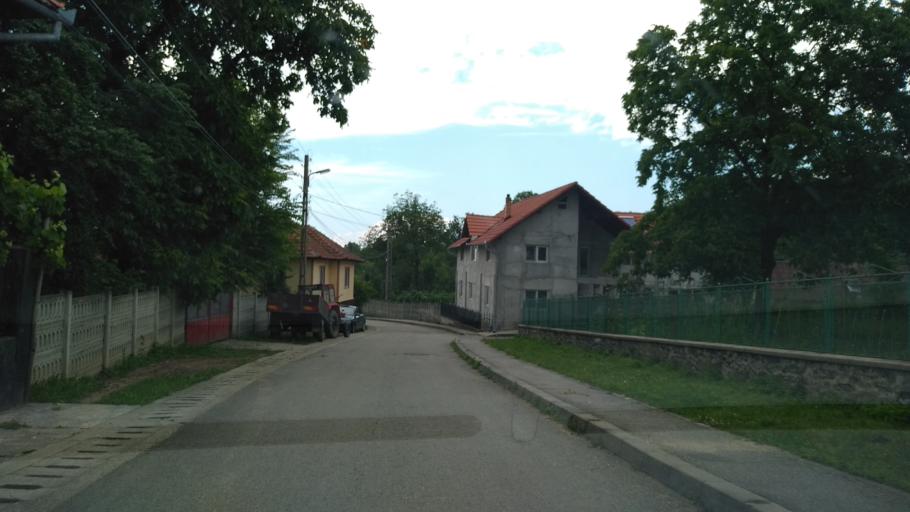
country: RO
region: Hunedoara
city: Salasu de Sus
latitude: 45.4869
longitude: 22.9453
